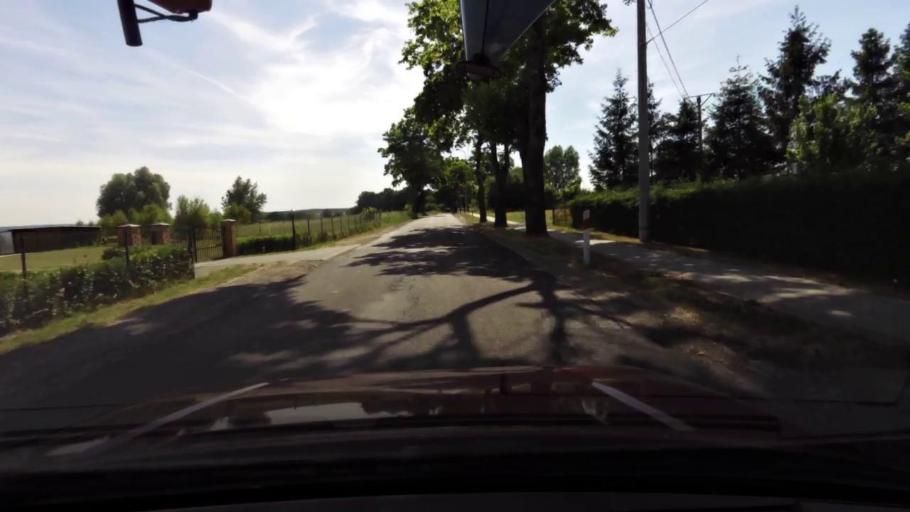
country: PL
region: Pomeranian Voivodeship
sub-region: Powiat slupski
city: Kobylnica
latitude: 54.3923
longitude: 16.9821
